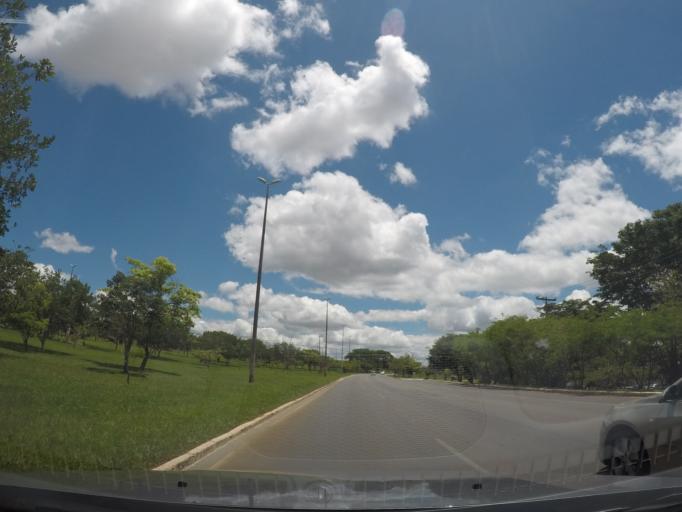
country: BR
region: Federal District
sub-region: Brasilia
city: Brasilia
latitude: -15.8216
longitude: -47.8832
